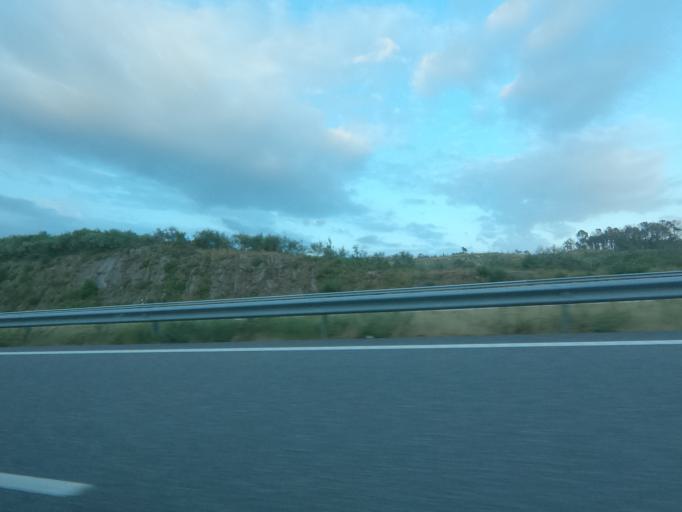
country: ES
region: Galicia
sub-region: Provincia de Ourense
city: Melon
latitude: 42.2351
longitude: -8.2309
